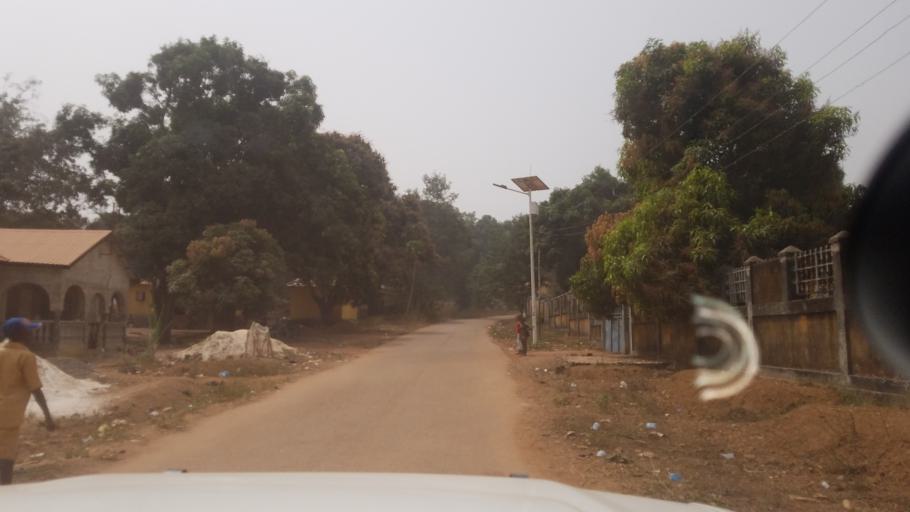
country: GN
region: Kindia
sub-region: Prefecture de Dubreka
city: Dubreka
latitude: 9.7881
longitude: -13.5114
